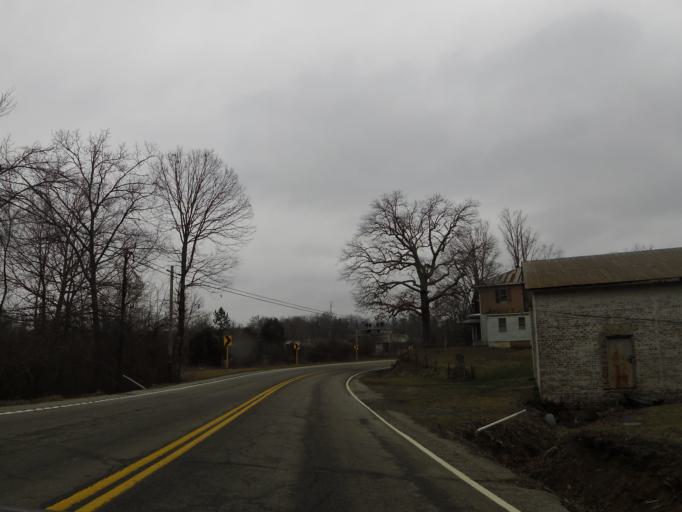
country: US
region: Tennessee
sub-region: Scott County
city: Huntsville
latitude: 36.3313
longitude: -84.6090
